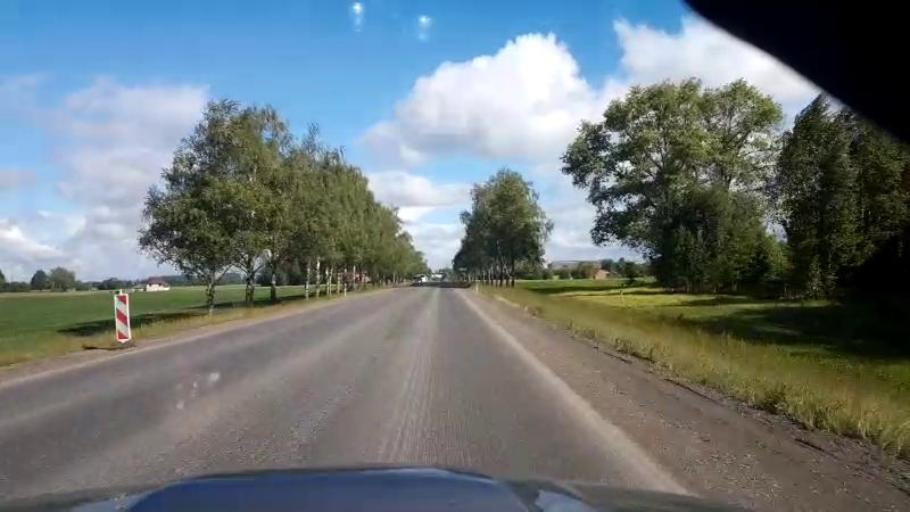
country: LV
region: Bauskas Rajons
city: Bauska
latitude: 56.3580
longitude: 24.2840
